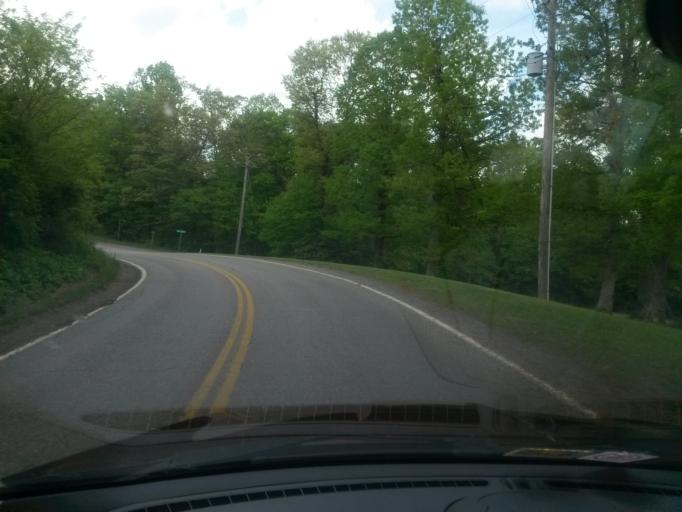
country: US
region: Virginia
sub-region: Floyd County
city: Floyd
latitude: 36.7682
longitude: -80.3863
